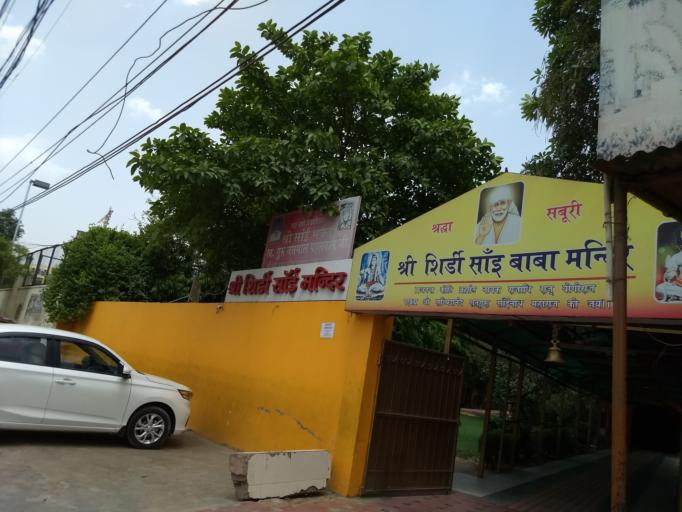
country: IN
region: Haryana
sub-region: Gurgaon
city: Gurgaon
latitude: 28.4943
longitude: 77.1038
